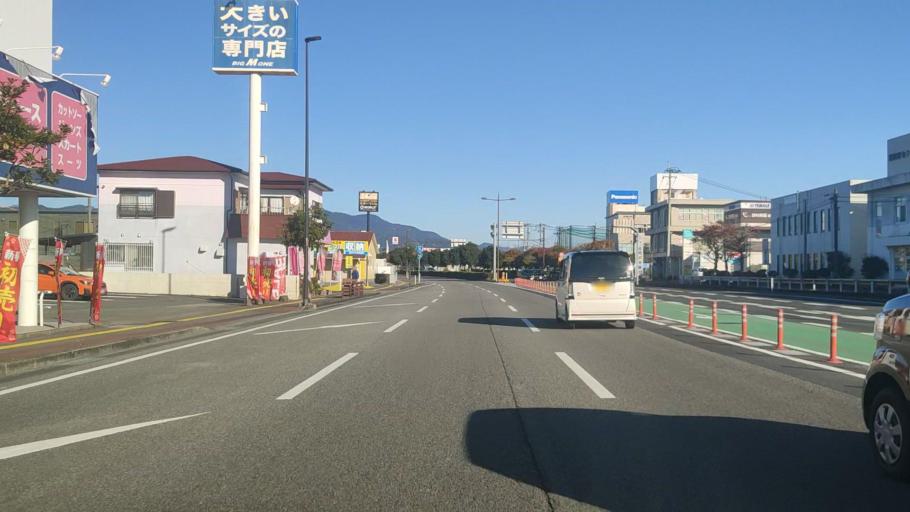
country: JP
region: Miyazaki
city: Nobeoka
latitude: 32.5763
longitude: 131.6835
